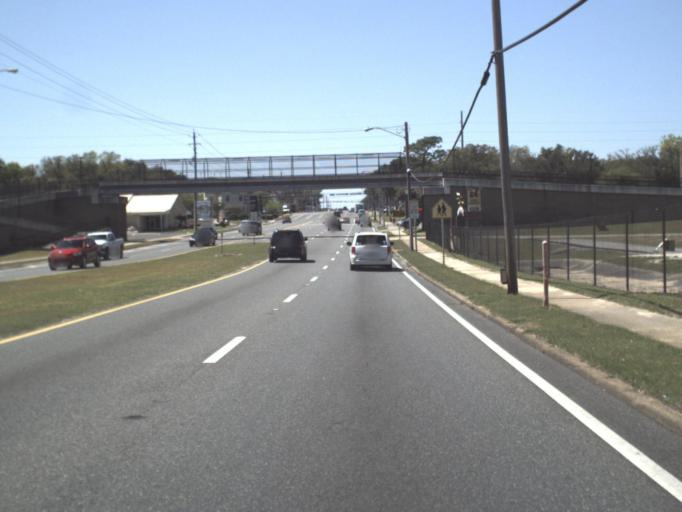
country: US
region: Florida
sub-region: Okaloosa County
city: Niceville
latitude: 30.5182
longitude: -86.4755
